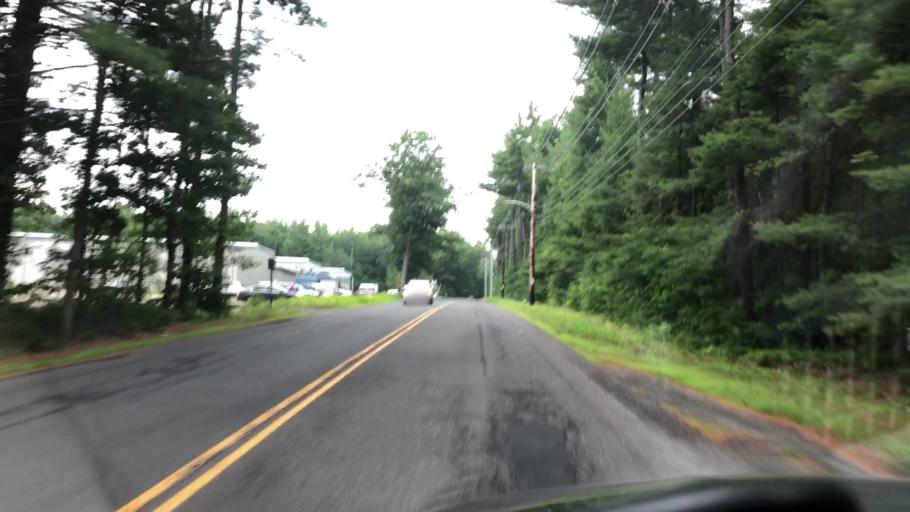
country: US
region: Massachusetts
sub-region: Hampden County
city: Westfield
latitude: 42.1771
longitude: -72.7491
